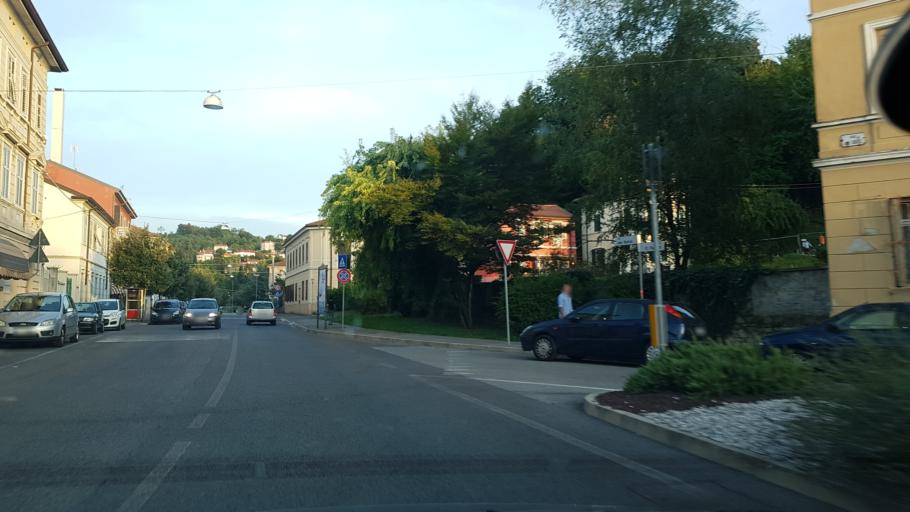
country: IT
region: Friuli Venezia Giulia
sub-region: Provincia di Gorizia
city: Gorizia
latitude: 45.9480
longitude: 13.6303
